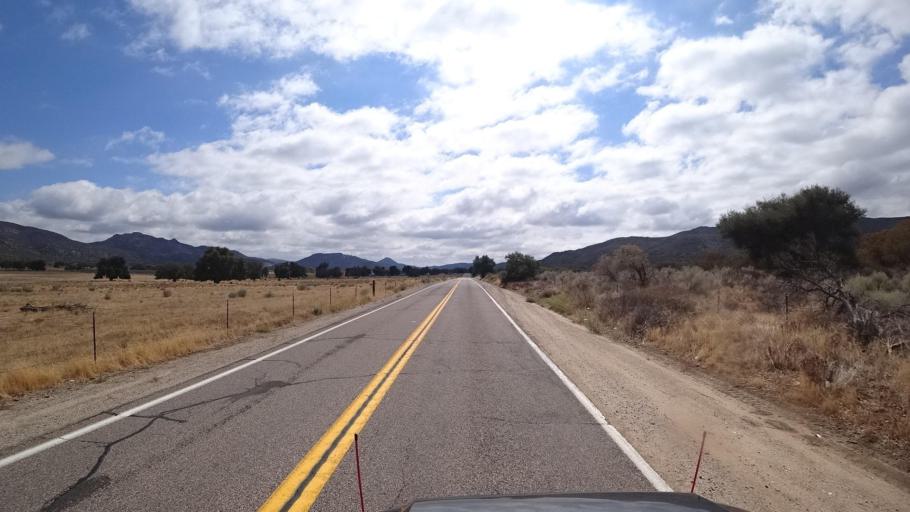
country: US
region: California
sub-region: San Diego County
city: Pine Valley
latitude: 32.7547
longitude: -116.4935
